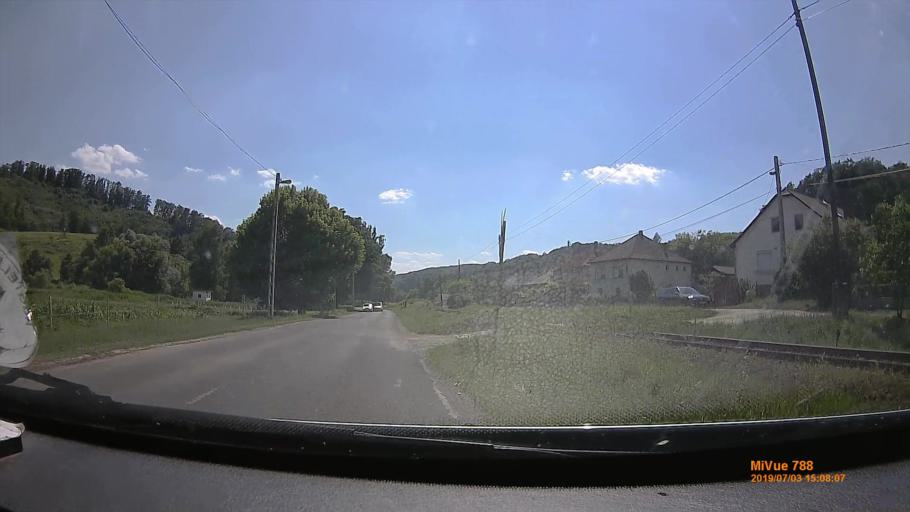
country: HU
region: Borsod-Abauj-Zemplen
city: Putnok
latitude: 48.2470
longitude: 20.3844
